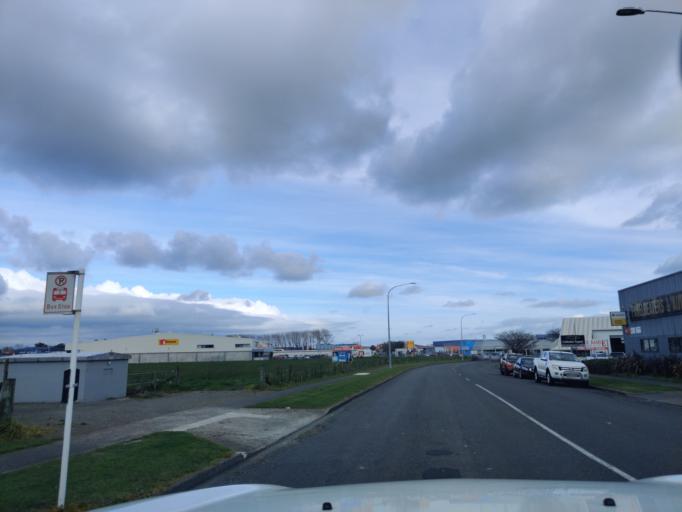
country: NZ
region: Manawatu-Wanganui
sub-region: Palmerston North City
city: Palmerston North
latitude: -40.3378
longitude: 175.6030
